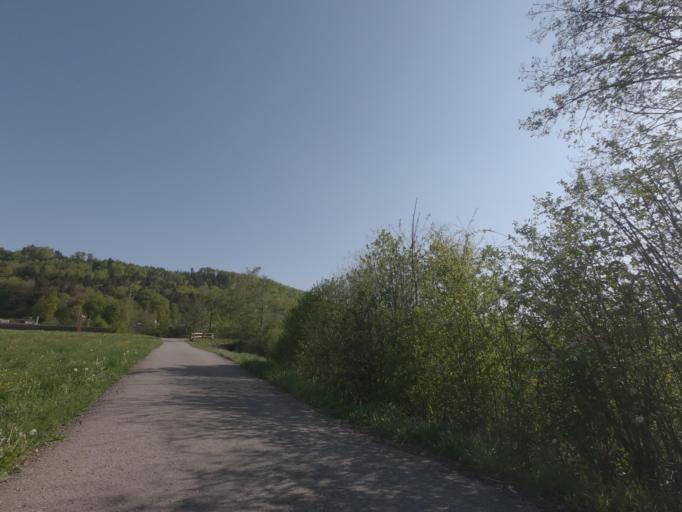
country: CH
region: Bern
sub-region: Biel/Bienne District
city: Orpund
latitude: 47.1639
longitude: 7.2999
